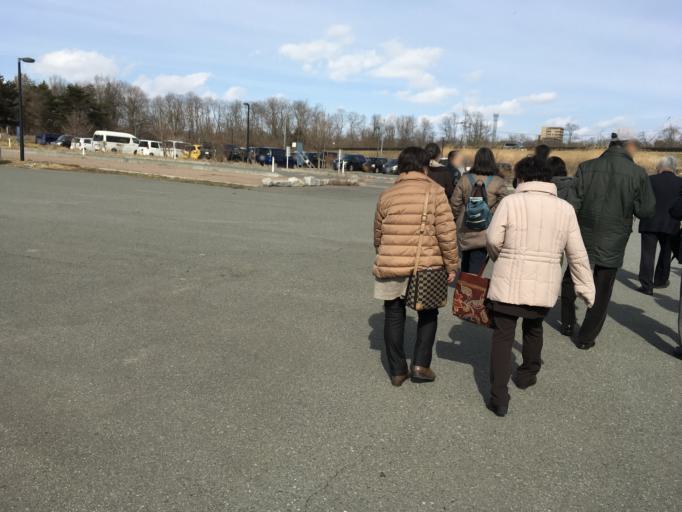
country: JP
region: Iwate
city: Morioka-shi
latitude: 39.6945
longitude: 141.1275
